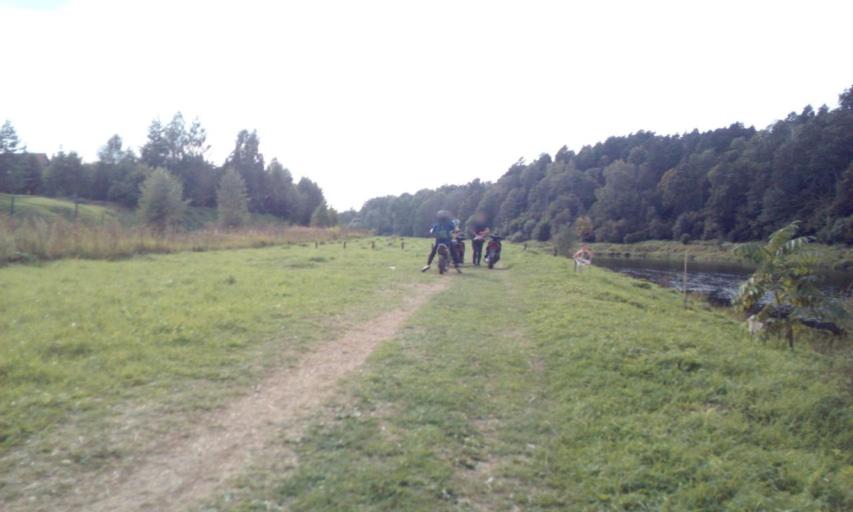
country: RU
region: Moskovskaya
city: Kolyubakino
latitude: 55.6066
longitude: 36.5381
